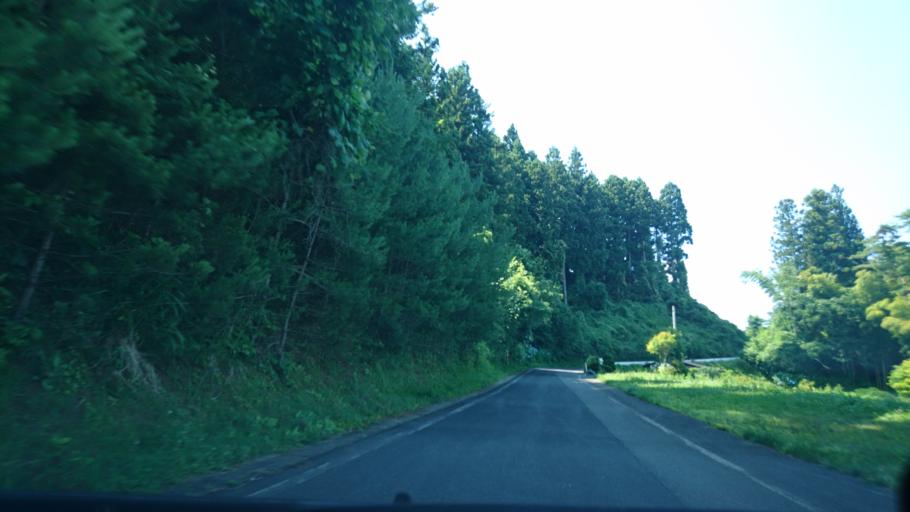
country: JP
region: Iwate
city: Ichinoseki
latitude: 38.9737
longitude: 141.1926
